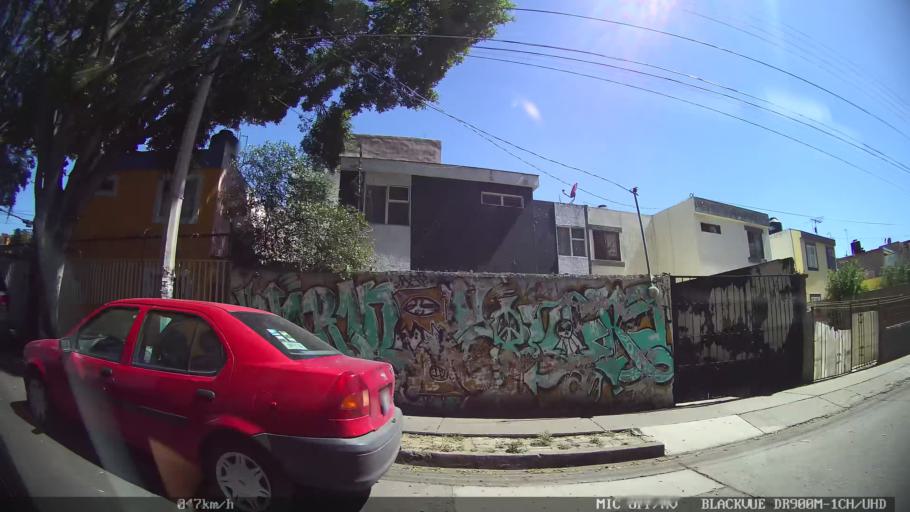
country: MX
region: Jalisco
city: Tlaquepaque
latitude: 20.6487
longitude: -103.2960
